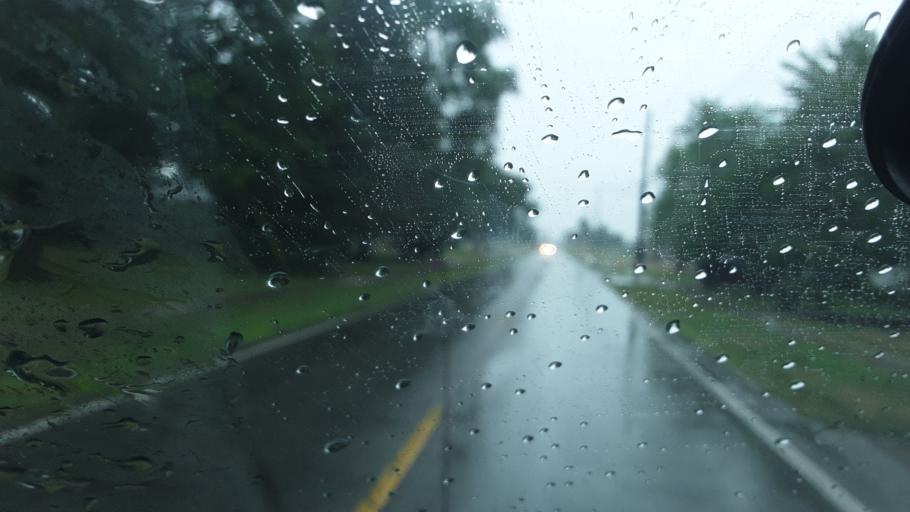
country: US
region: Ohio
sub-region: Williams County
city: Montpelier
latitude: 41.5719
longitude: -84.6100
